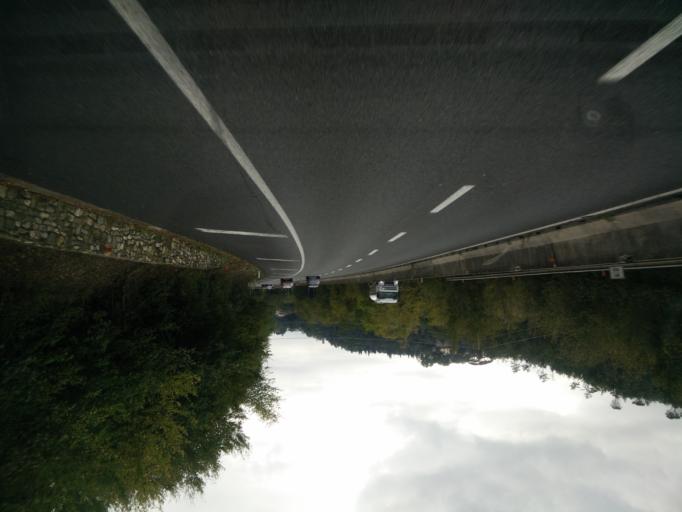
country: IT
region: Tuscany
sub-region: Province of Florence
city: Tavarnuzze
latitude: 43.6979
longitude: 11.2118
